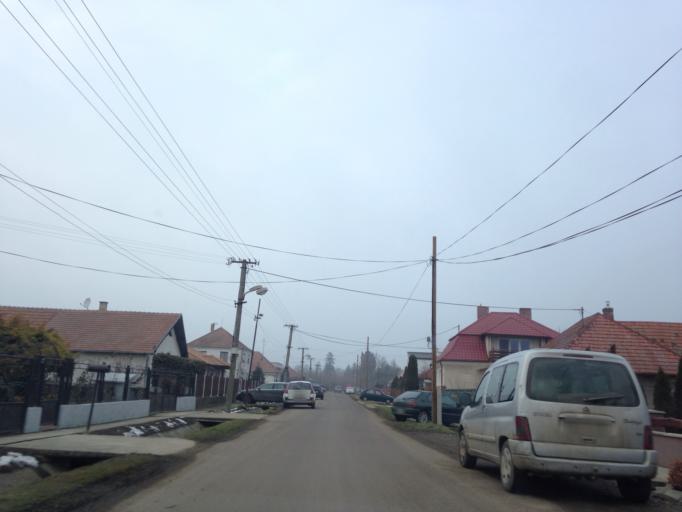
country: SK
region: Nitriansky
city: Svodin
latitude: 47.9886
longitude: 18.3940
